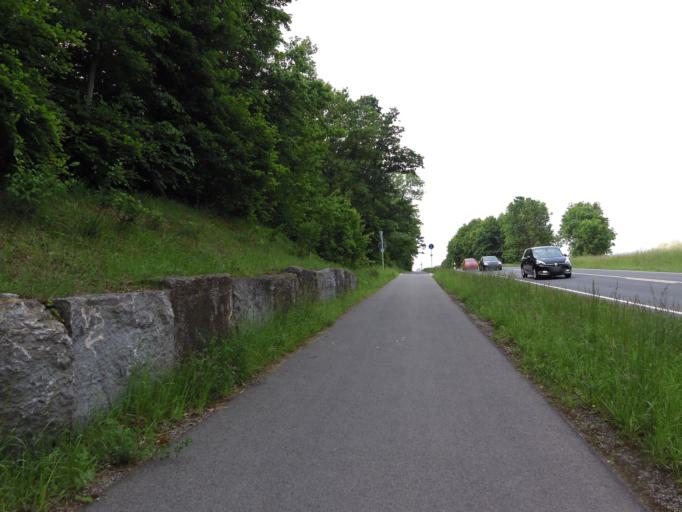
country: DE
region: Bavaria
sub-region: Regierungsbezirk Unterfranken
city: Kist
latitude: 49.7546
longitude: 9.8489
